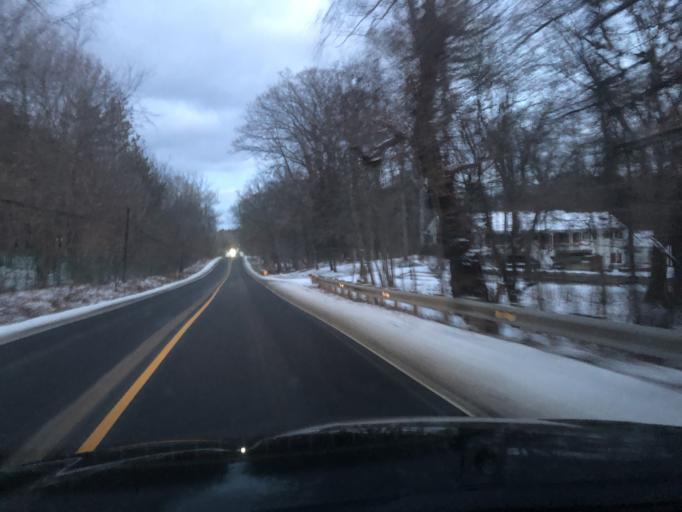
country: US
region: Michigan
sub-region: Oakland County
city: Milford
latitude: 42.5789
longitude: -83.6366
